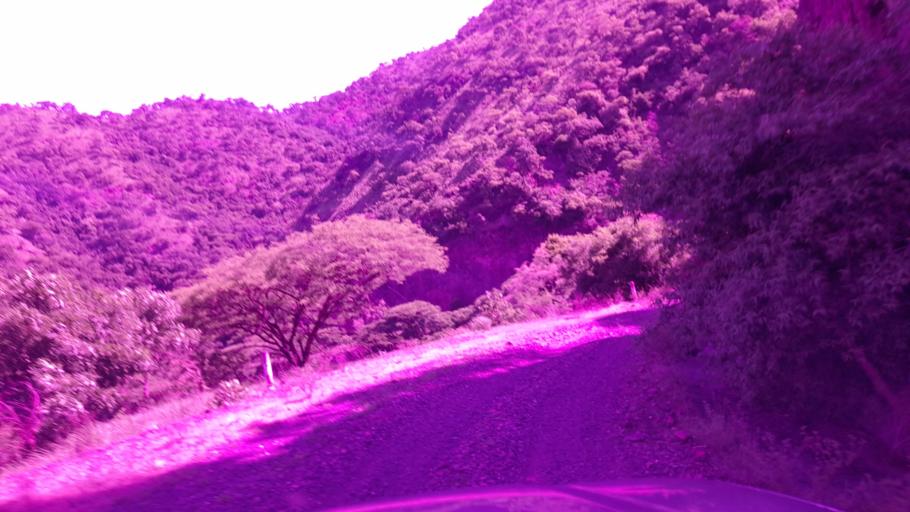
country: ET
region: Southern Nations, Nationalities, and People's Region
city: K'olito
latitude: 7.7755
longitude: 37.5550
